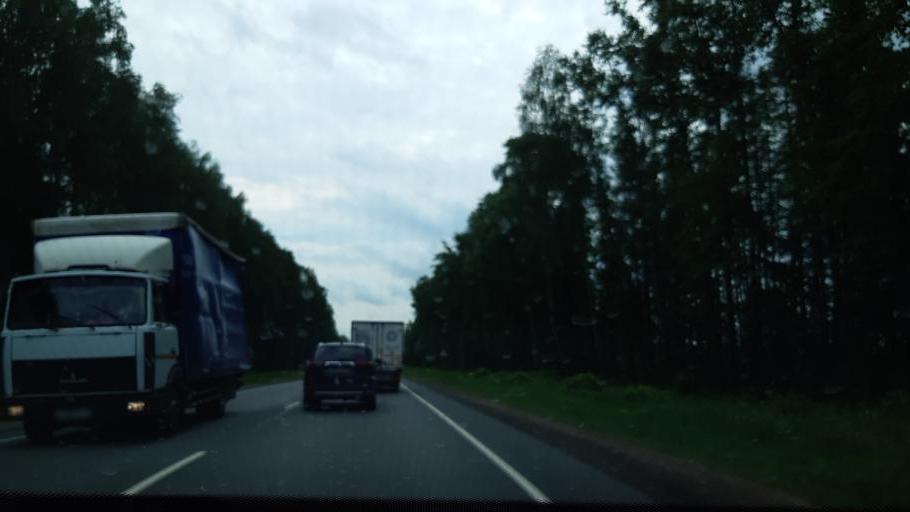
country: RU
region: Moskovskaya
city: Dorokhovo
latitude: 55.5157
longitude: 36.3510
